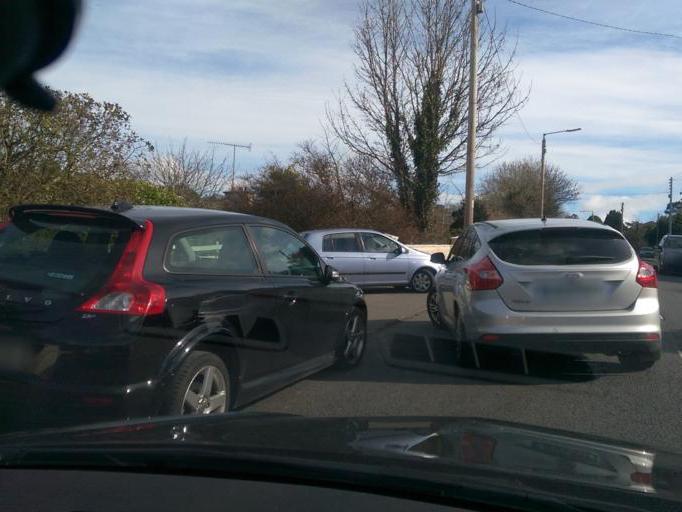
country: IE
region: Leinster
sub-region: Fingal County
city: Howth
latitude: 53.3825
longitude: -6.0599
